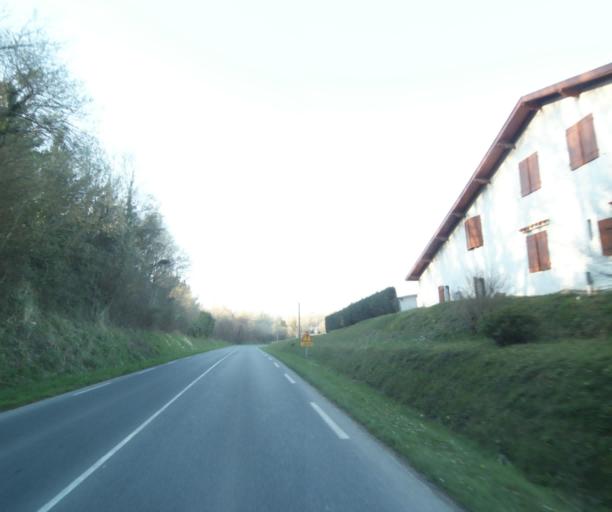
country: FR
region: Aquitaine
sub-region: Departement des Pyrenees-Atlantiques
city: Urrugne
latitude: 43.3574
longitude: -1.6916
